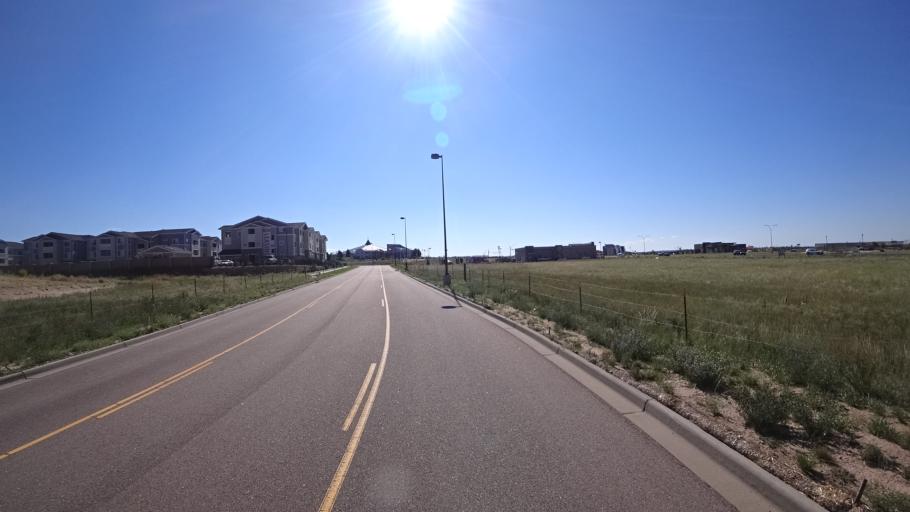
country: US
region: Colorado
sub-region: El Paso County
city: Gleneagle
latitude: 38.9920
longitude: -104.8016
